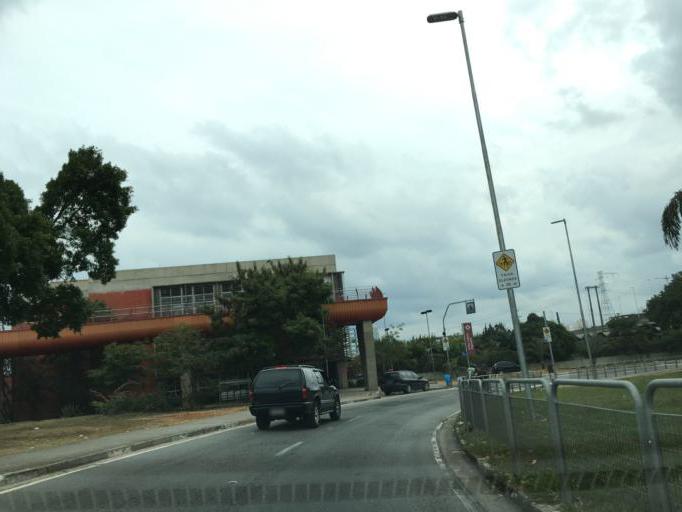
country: BR
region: Sao Paulo
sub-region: Osasco
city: Osasco
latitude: -23.5453
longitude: -46.7323
